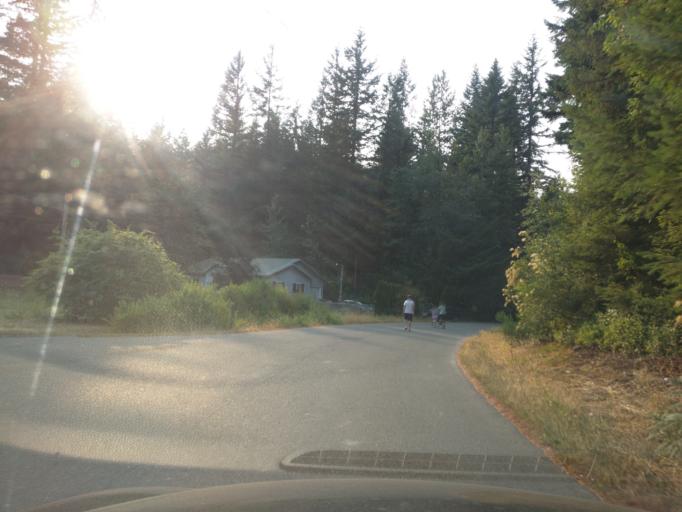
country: US
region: Washington
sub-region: Whatcom County
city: Peaceful Valley
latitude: 48.9434
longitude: -122.1490
